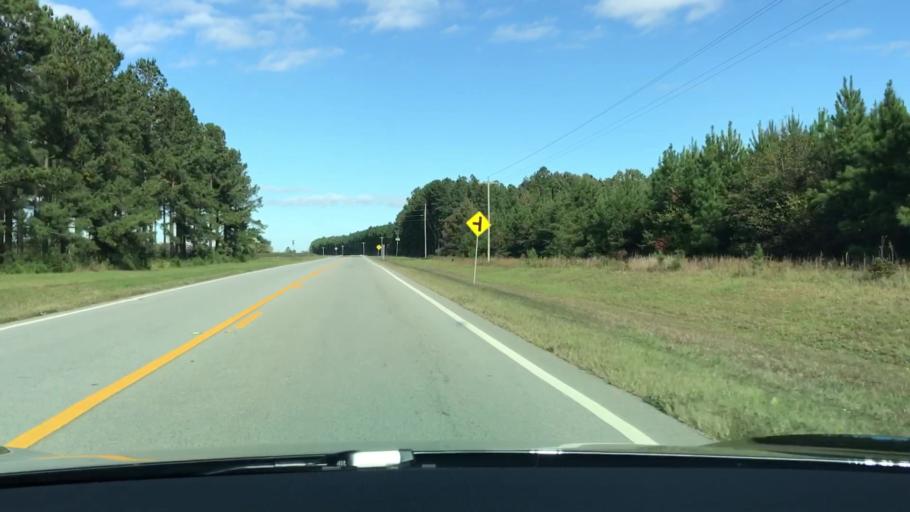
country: US
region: Georgia
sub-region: Glascock County
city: Gibson
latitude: 33.2811
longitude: -82.5043
